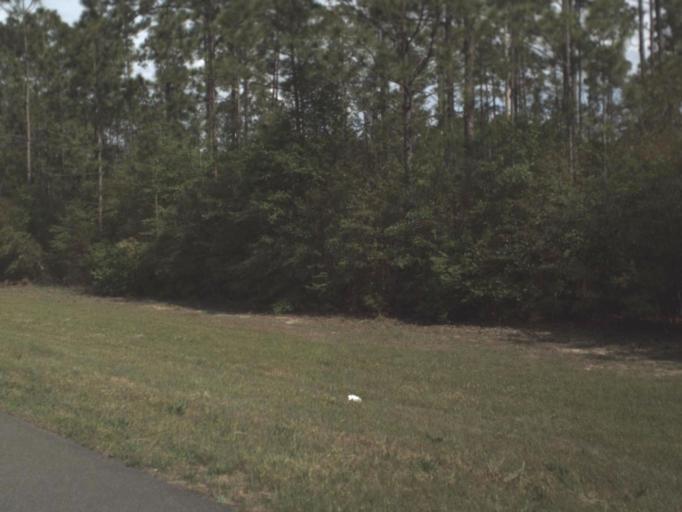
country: US
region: Florida
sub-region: Santa Rosa County
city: East Milton
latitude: 30.6921
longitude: -86.8104
